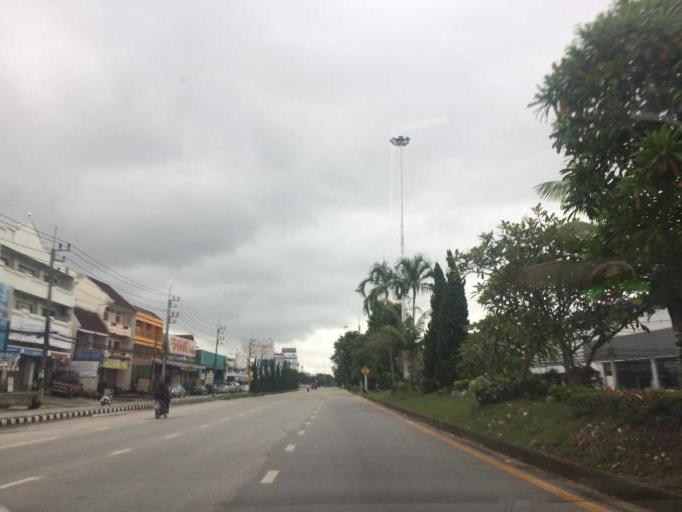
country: TH
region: Chiang Rai
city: Chiang Rai
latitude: 19.8992
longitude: 99.8392
